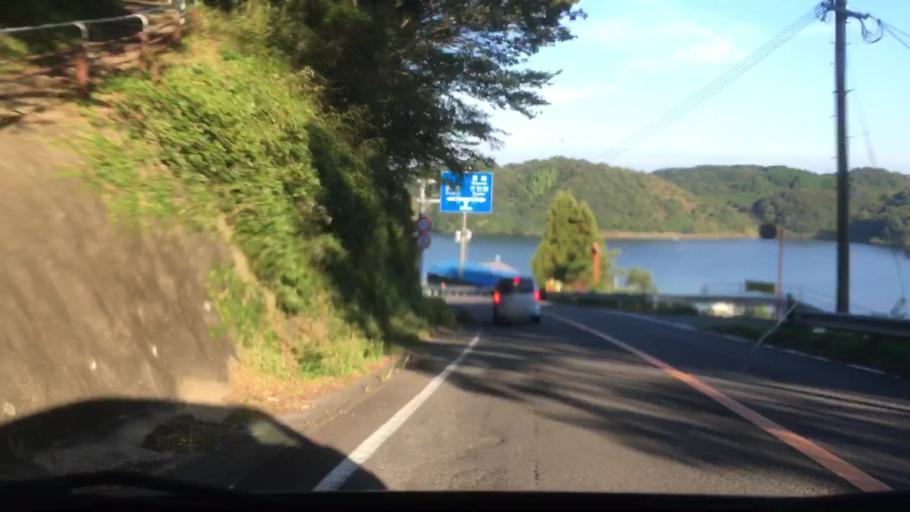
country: JP
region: Nagasaki
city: Sasebo
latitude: 33.0487
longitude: 129.7266
